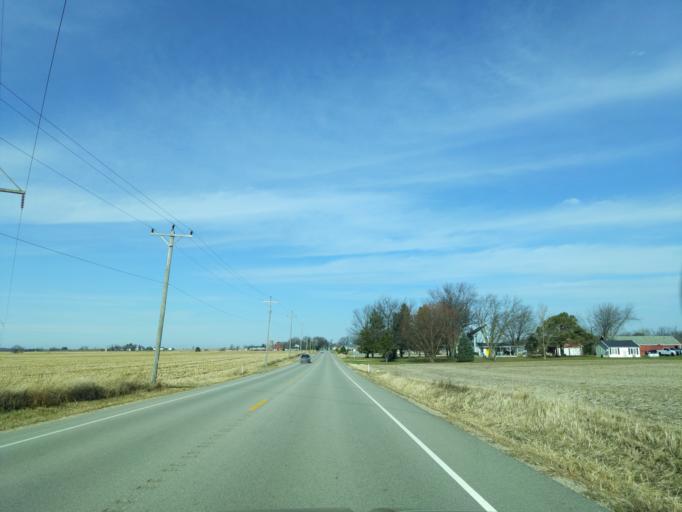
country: US
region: Wisconsin
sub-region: Walworth County
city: Elkhorn
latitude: 42.7211
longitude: -88.5819
